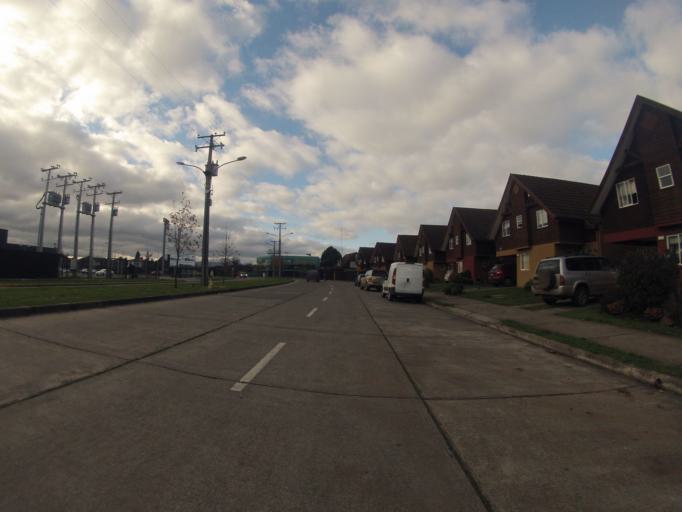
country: CL
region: Araucania
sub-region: Provincia de Cautin
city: Temuco
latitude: -38.7415
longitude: -72.6424
